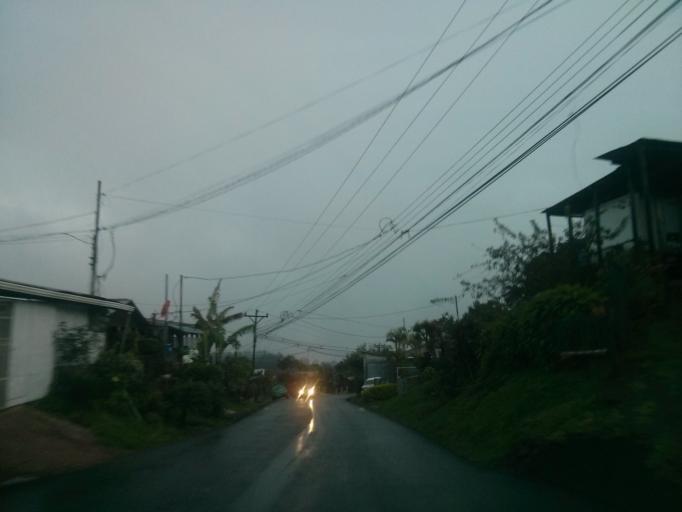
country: CR
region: Alajuela
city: Sabanilla
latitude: 10.1051
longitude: -84.1923
